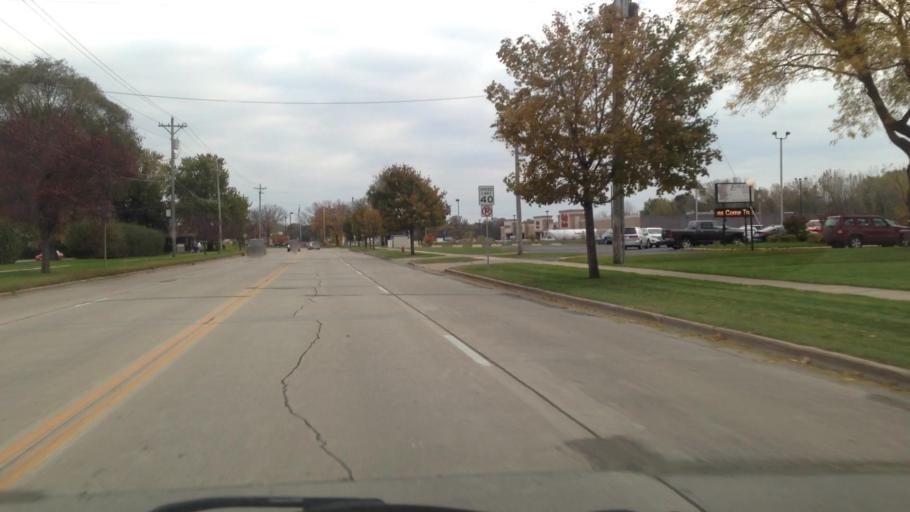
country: US
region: Minnesota
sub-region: Olmsted County
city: Rochester
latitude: 44.0127
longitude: -92.4446
